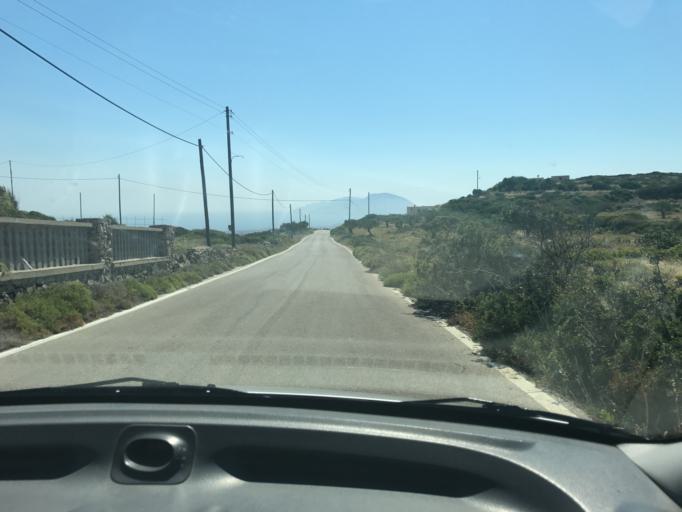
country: GR
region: South Aegean
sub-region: Nomos Dodekanisou
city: Karpathos
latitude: 35.4790
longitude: 27.1524
